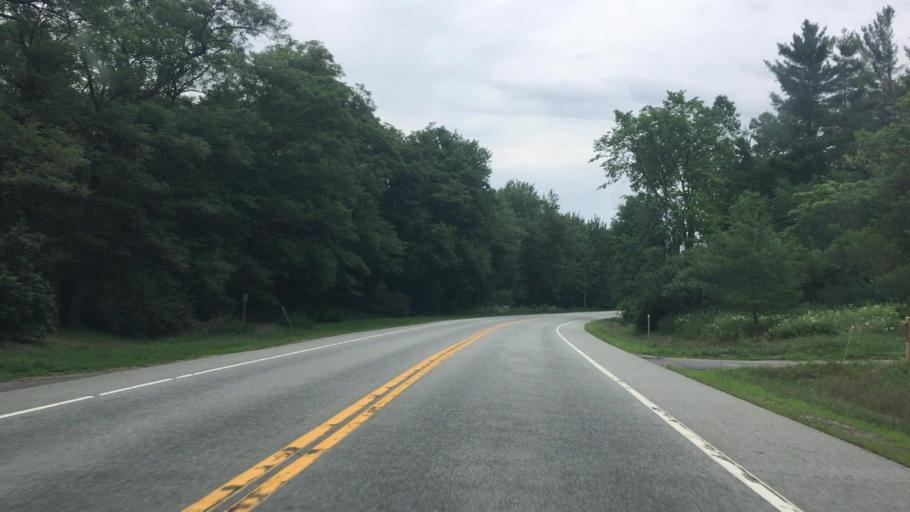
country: US
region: New York
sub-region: Essex County
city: Lake Placid
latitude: 44.3208
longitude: -73.7798
